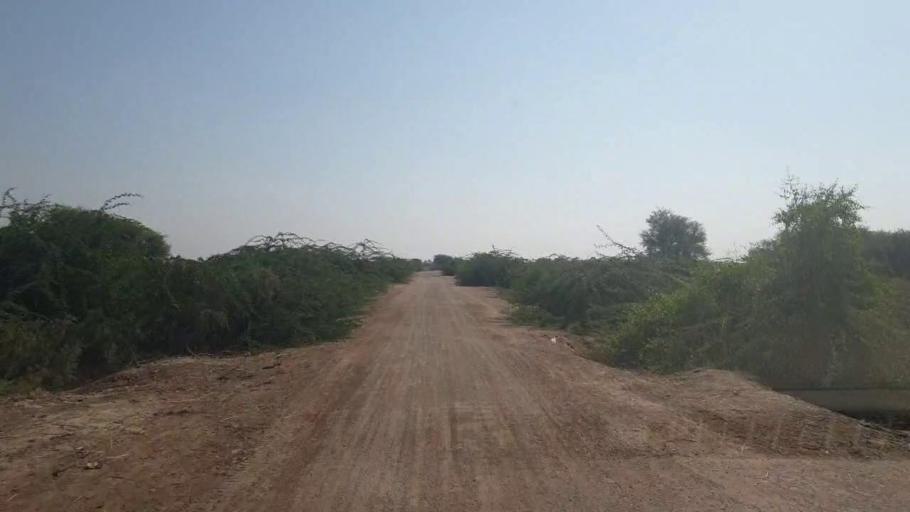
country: PK
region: Sindh
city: Badin
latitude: 24.5625
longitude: 68.8458
